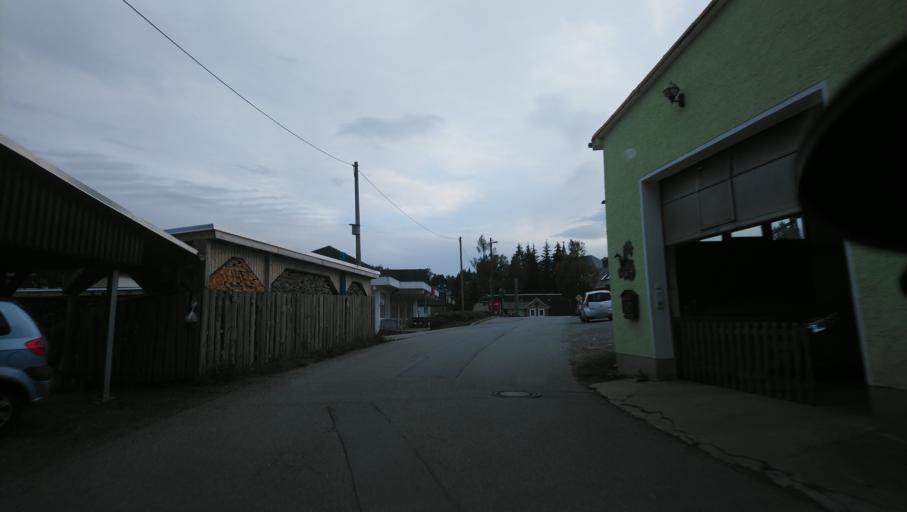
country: DE
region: Saxony
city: Barenstein
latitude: 50.4990
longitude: 13.0251
